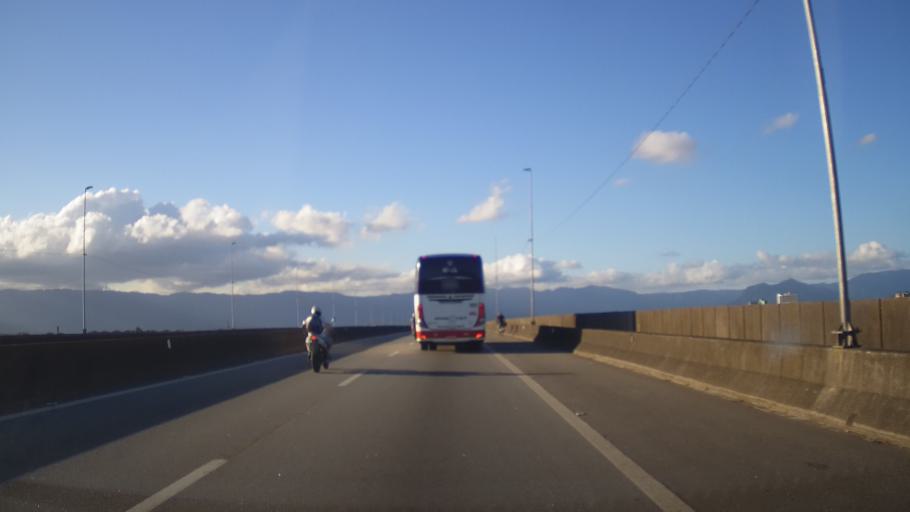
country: BR
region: Sao Paulo
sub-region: Sao Vicente
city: Sao Vicente
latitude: -23.9821
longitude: -46.4008
